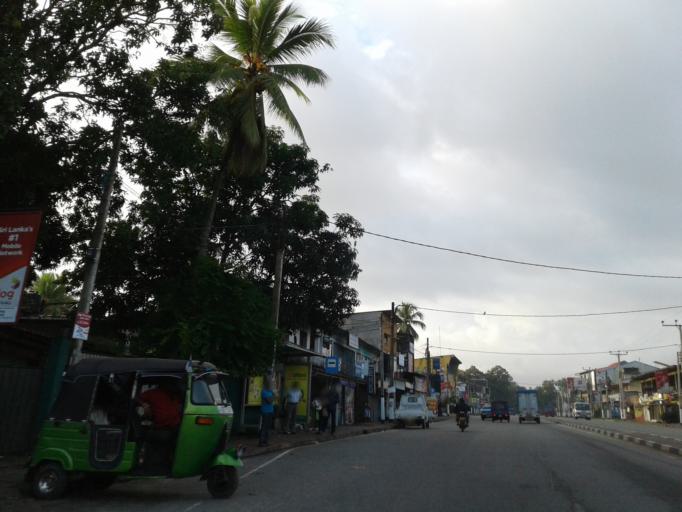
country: LK
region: Western
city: Mulleriyawa
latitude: 6.9411
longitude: 79.9872
